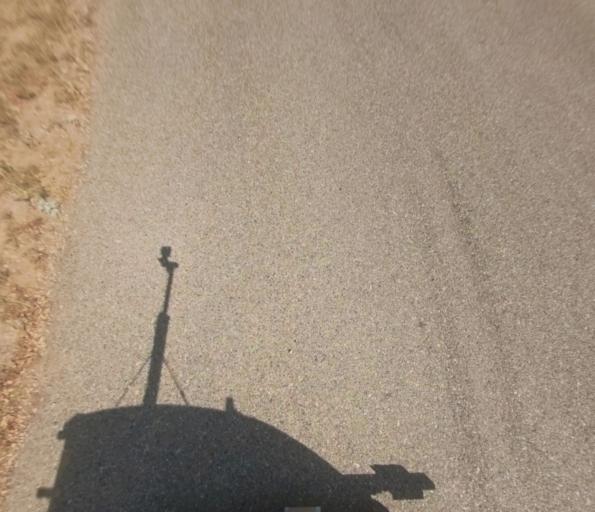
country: US
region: California
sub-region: Madera County
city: Yosemite Lakes
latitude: 37.2658
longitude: -119.8594
